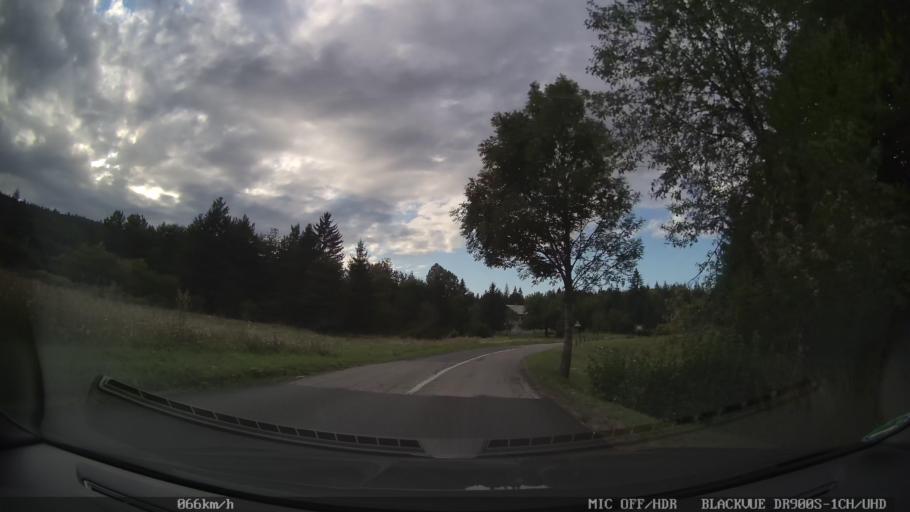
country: HR
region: Licko-Senjska
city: Jezerce
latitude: 44.9574
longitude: 15.5259
